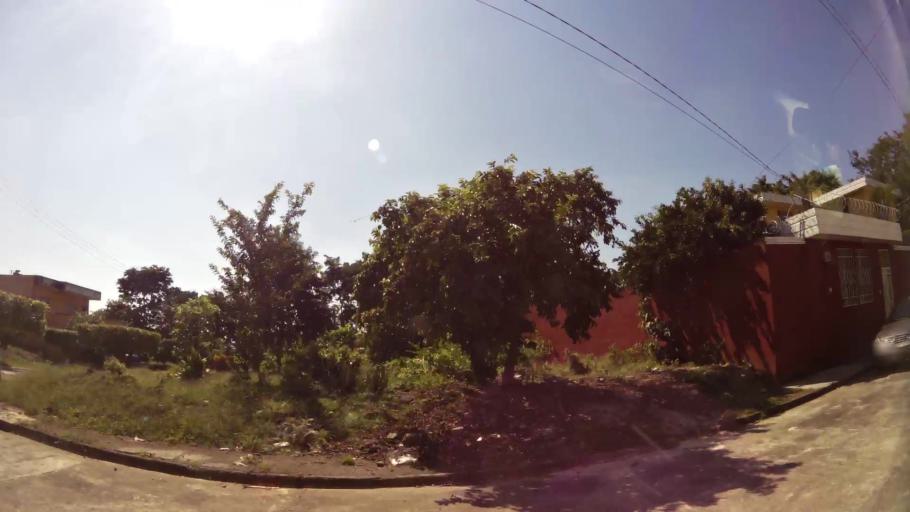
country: GT
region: Suchitepeque
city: Mazatenango
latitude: 14.5486
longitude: -91.5063
